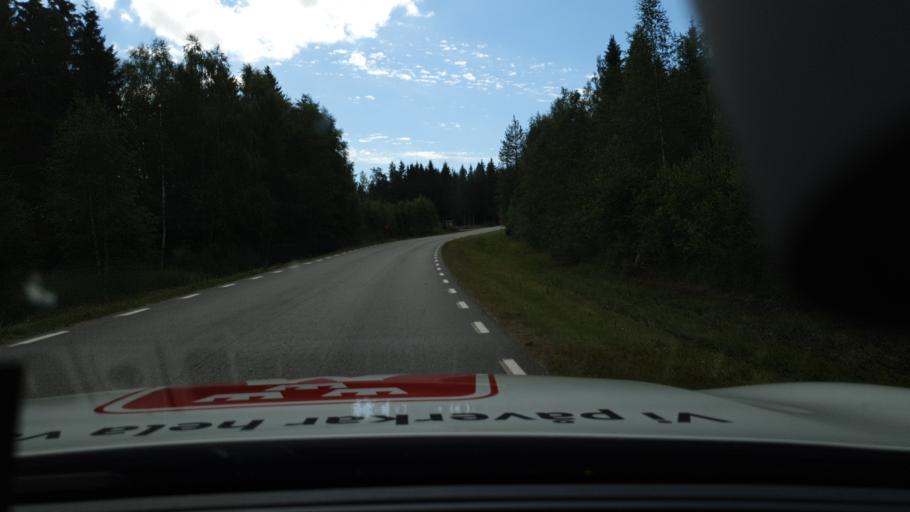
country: SE
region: Norrbotten
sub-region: Kalix Kommun
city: Toere
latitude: 65.8521
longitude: 22.6796
